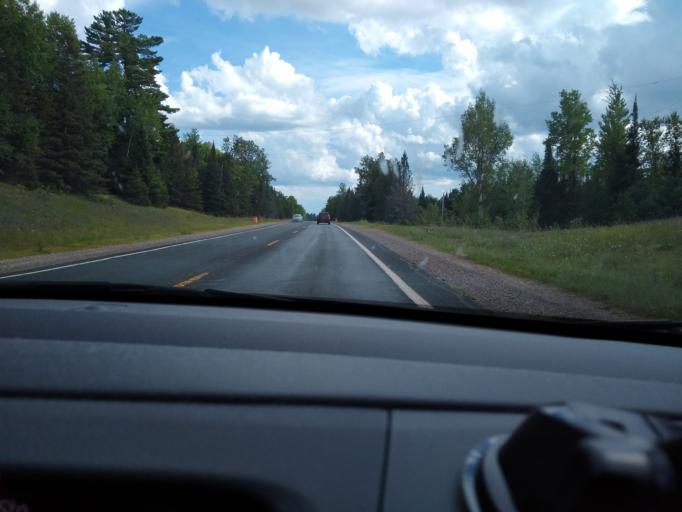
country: US
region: Michigan
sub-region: Iron County
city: Crystal Falls
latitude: 46.2685
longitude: -88.0174
